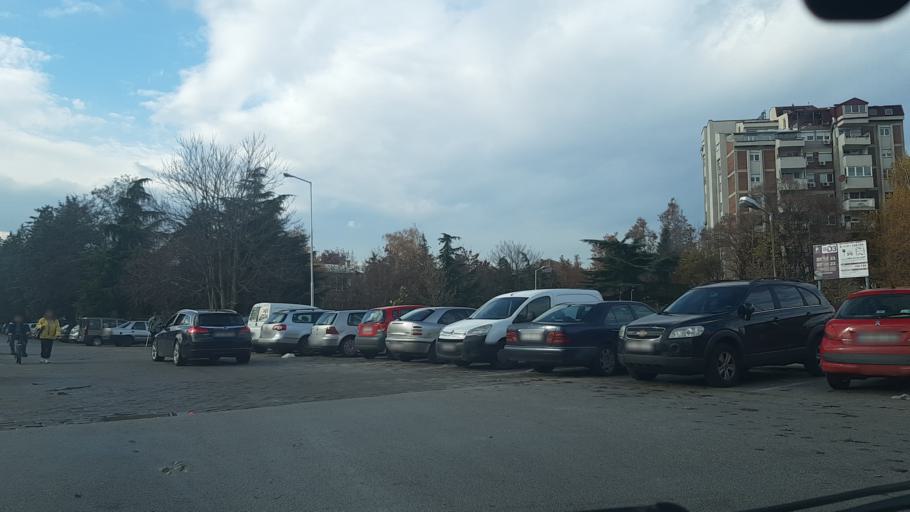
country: MK
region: Kisela Voda
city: Usje
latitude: 41.9840
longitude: 21.4620
